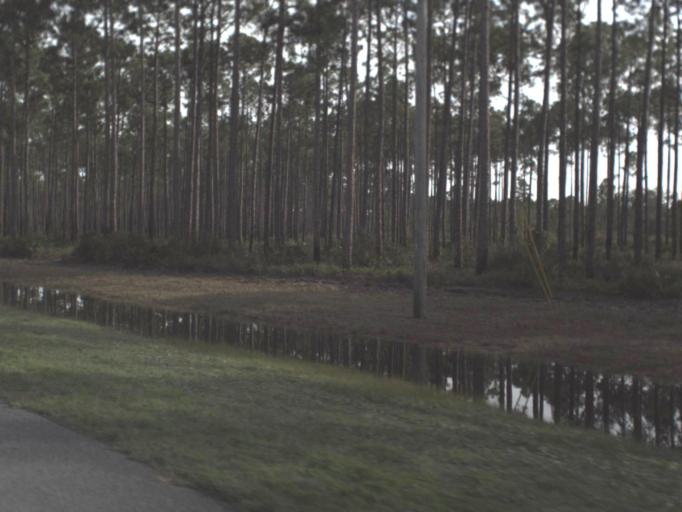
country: US
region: Florida
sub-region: Bay County
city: Mexico Beach
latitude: 29.9818
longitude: -85.4759
